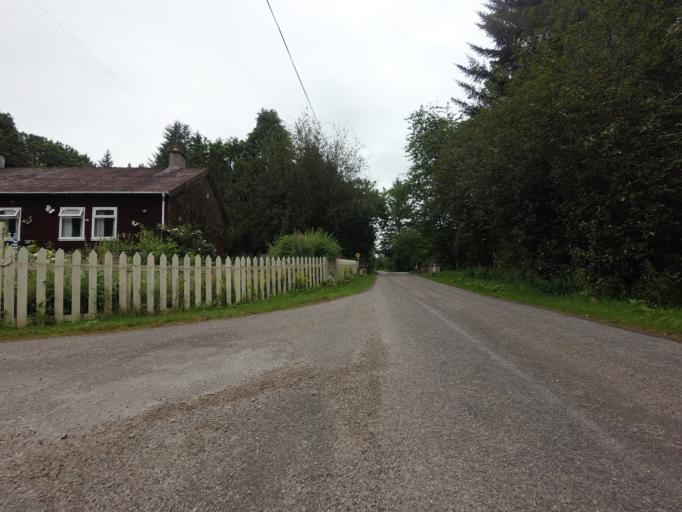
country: GB
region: Scotland
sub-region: Highland
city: Evanton
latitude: 57.9671
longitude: -4.4117
